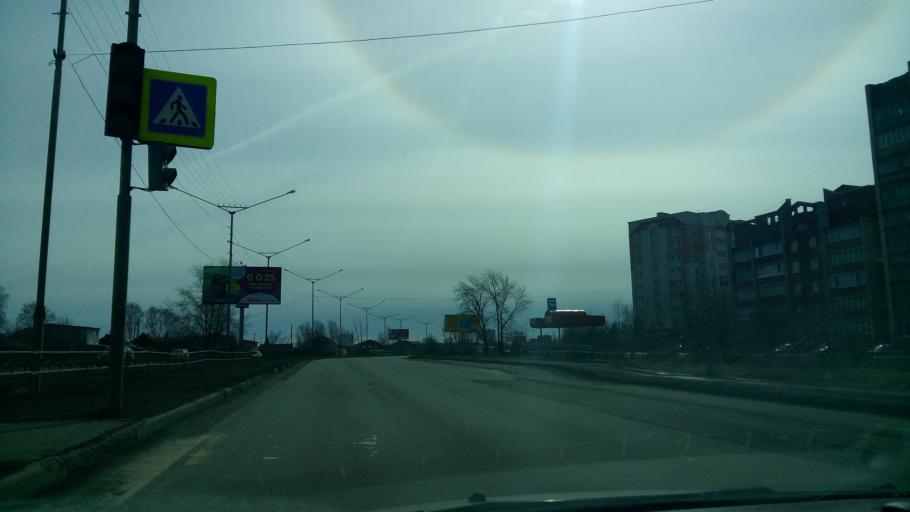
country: RU
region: Sverdlovsk
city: Nizhniy Tagil
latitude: 57.8977
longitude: 59.9390
